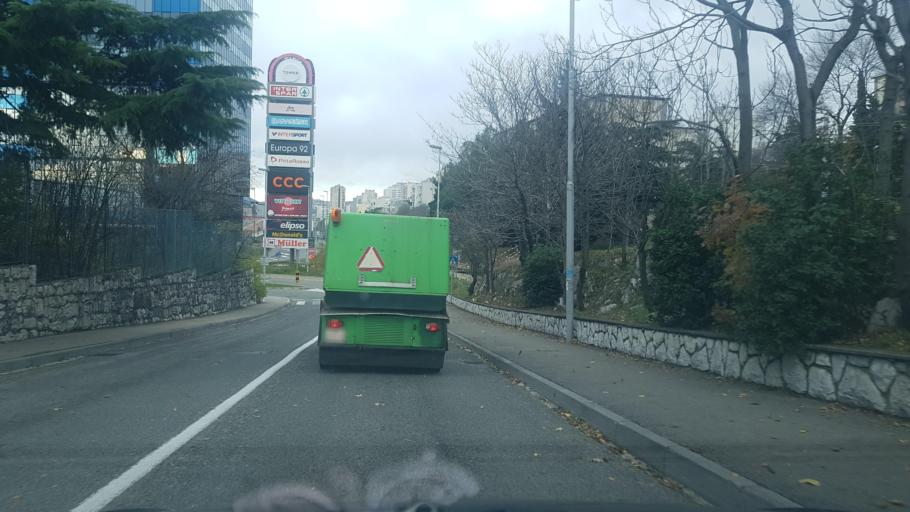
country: HR
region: Primorsko-Goranska
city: Cavle
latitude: 45.3171
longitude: 14.4714
